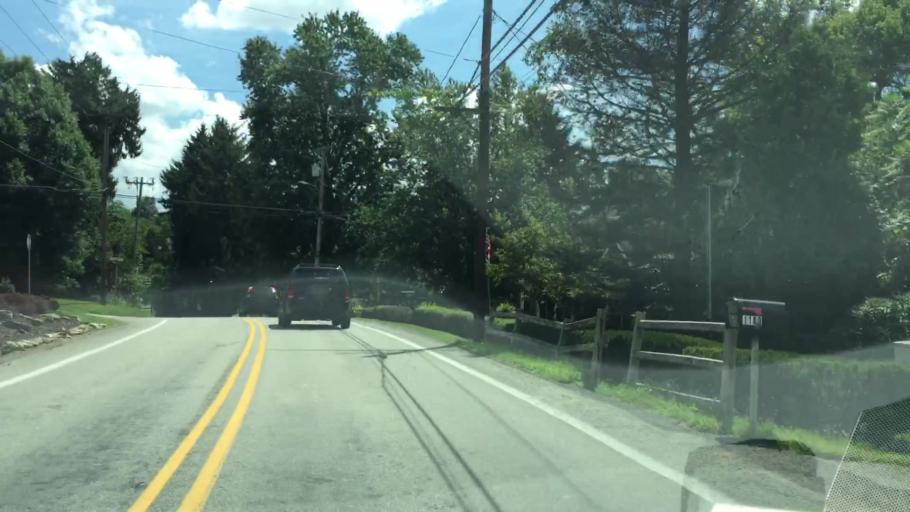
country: US
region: Pennsylvania
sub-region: Allegheny County
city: Bethel Park
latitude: 40.3118
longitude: -80.0350
